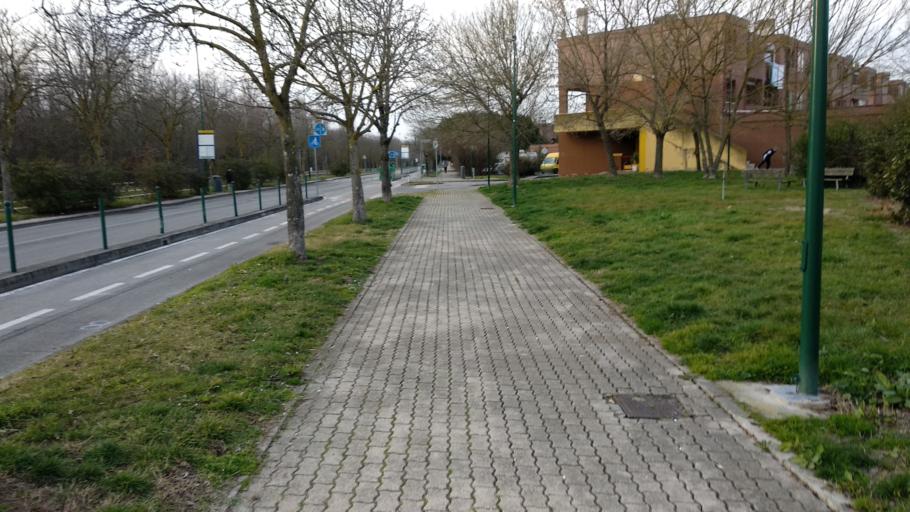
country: IT
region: Veneto
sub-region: Provincia di Venezia
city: Campalto
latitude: 45.4829
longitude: 12.2678
